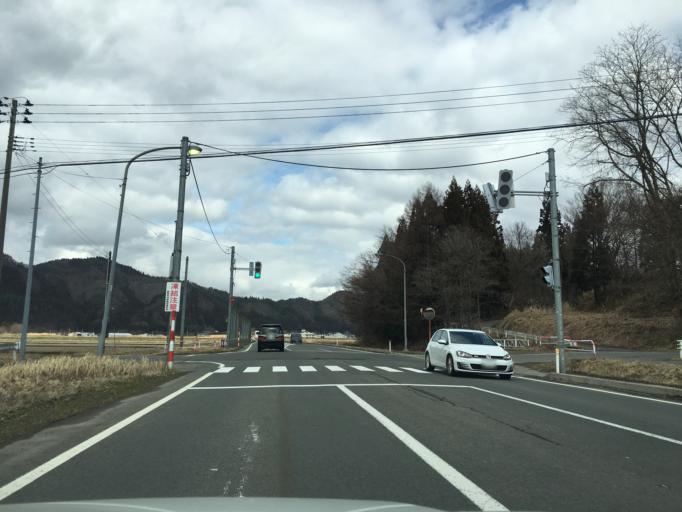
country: JP
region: Akita
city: Hanawa
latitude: 40.2359
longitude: 140.7359
